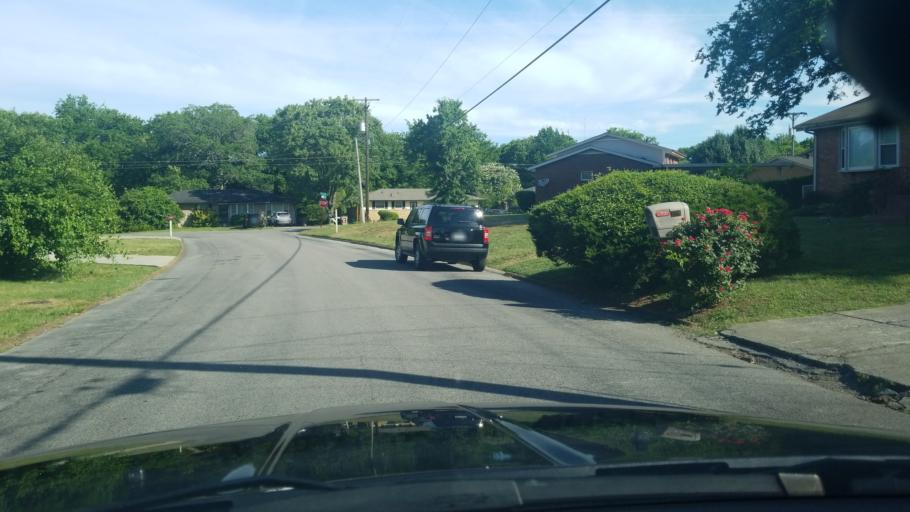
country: US
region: Tennessee
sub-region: Davidson County
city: Nashville
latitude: 36.2332
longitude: -86.7748
